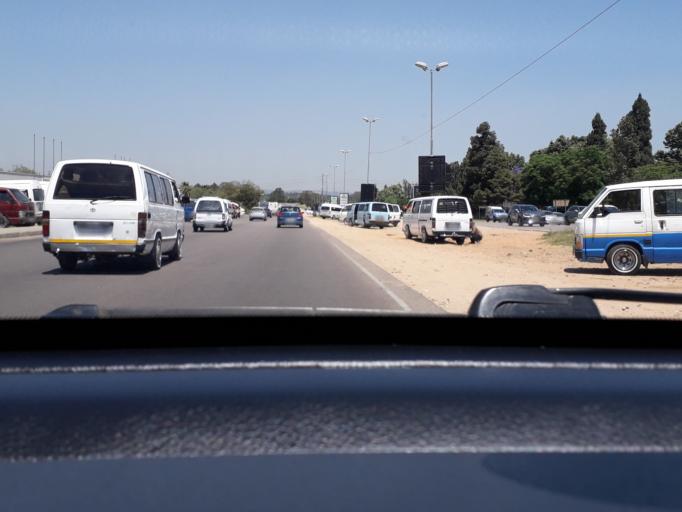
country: ZA
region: Gauteng
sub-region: City of Johannesburg Metropolitan Municipality
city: Midrand
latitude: -26.0570
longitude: 28.0905
